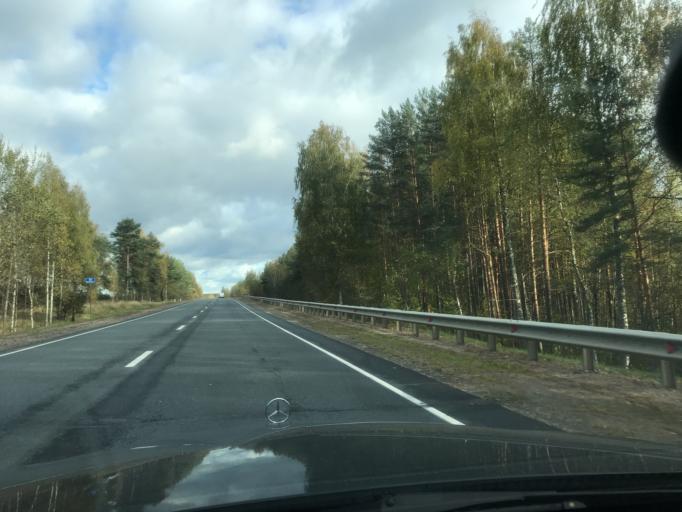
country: RU
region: Pskov
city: Pustoshka
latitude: 56.3329
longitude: 29.5985
